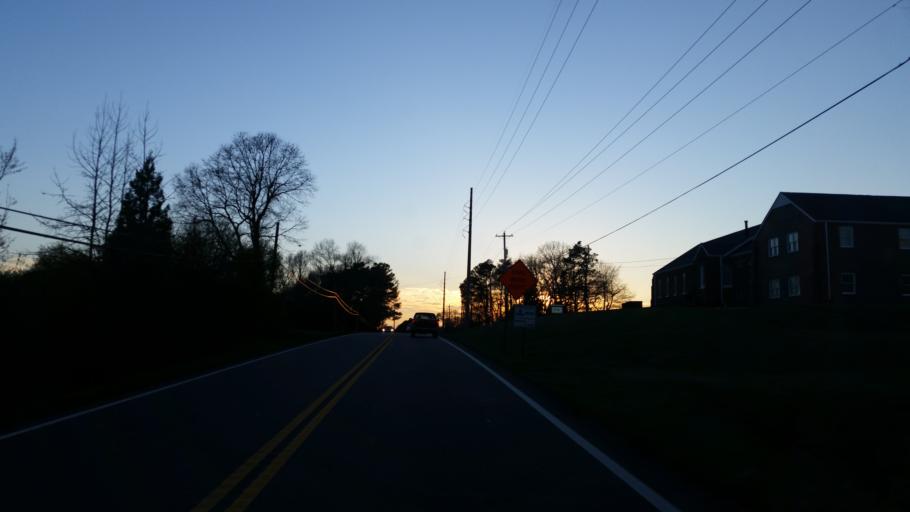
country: US
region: Georgia
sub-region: Hall County
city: Flowery Branch
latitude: 34.2925
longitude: -84.0071
